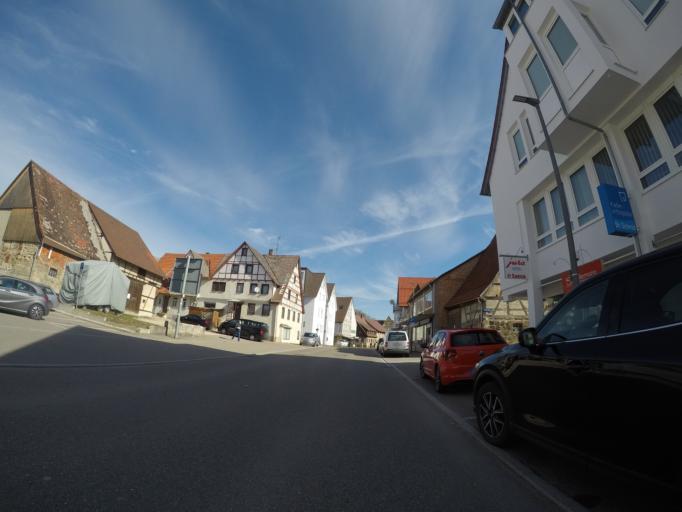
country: DE
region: Baden-Wuerttemberg
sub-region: Tuebingen Region
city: Laichingen
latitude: 48.4905
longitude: 9.6857
